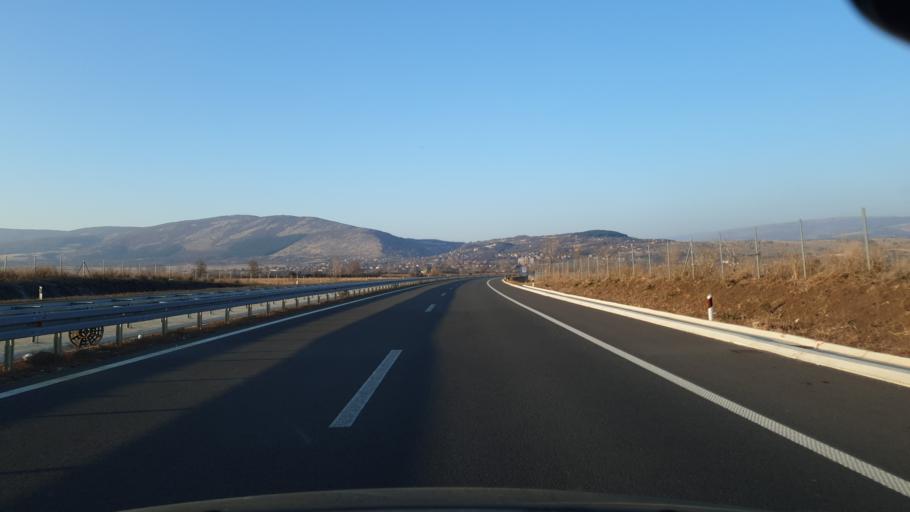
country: RS
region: Central Serbia
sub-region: Pirotski Okrug
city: Pirot
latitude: 43.1396
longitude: 22.5685
